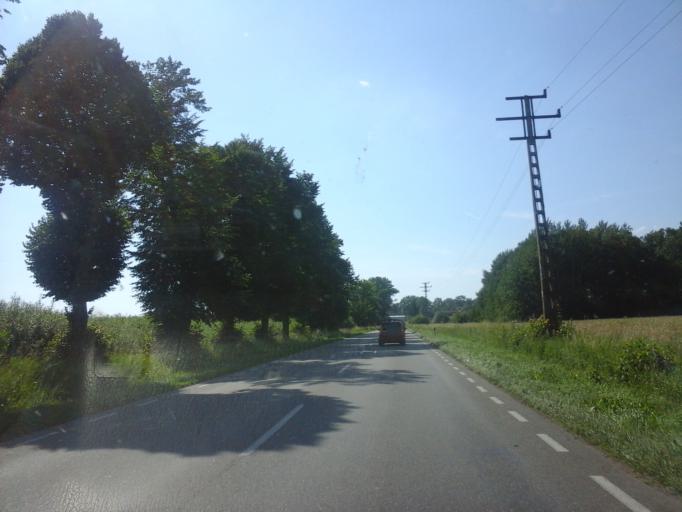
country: PL
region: West Pomeranian Voivodeship
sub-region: Powiat bialogardzki
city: Karlino
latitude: 54.0282
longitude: 15.9108
